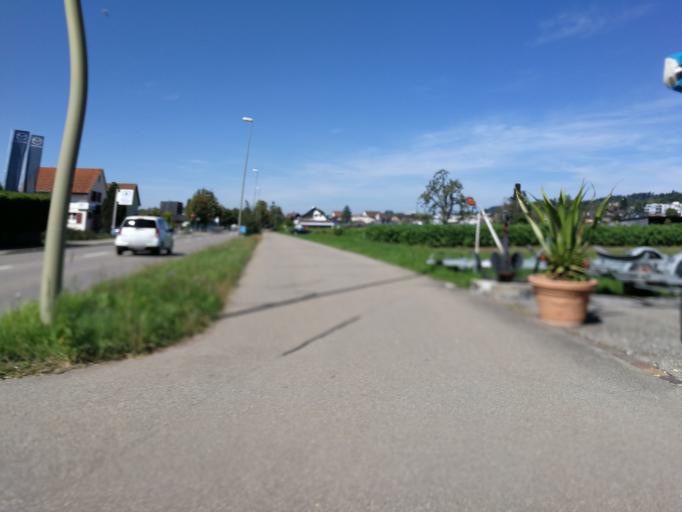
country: CH
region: Zurich
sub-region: Bezirk Pfaeffikon
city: Pfaeffikon / Irgenhausen
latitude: 47.3570
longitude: 8.7976
